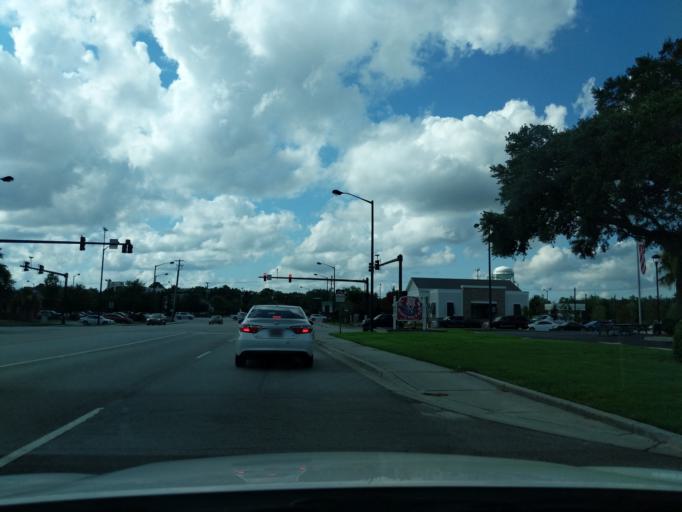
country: US
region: South Carolina
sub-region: Charleston County
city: Mount Pleasant
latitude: 32.8033
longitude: -79.8903
